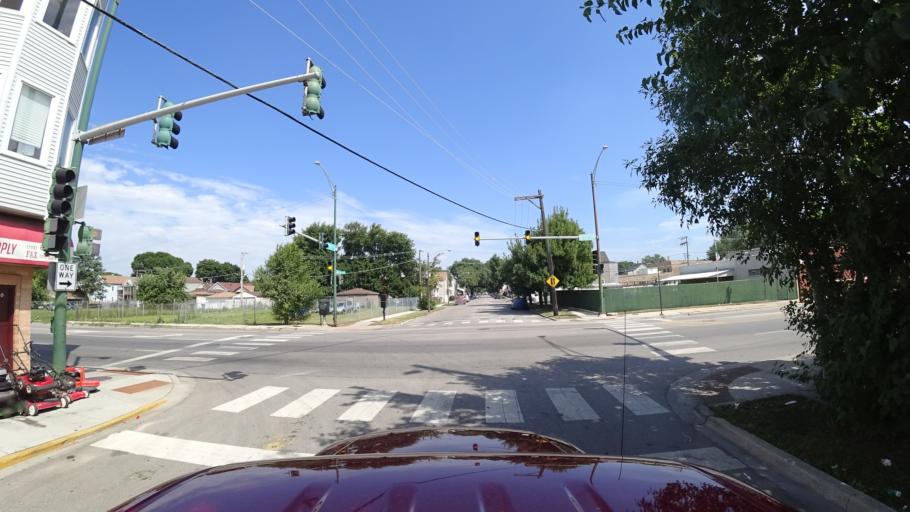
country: US
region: Illinois
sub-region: Cook County
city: Chicago
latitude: 41.8088
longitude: -87.6407
